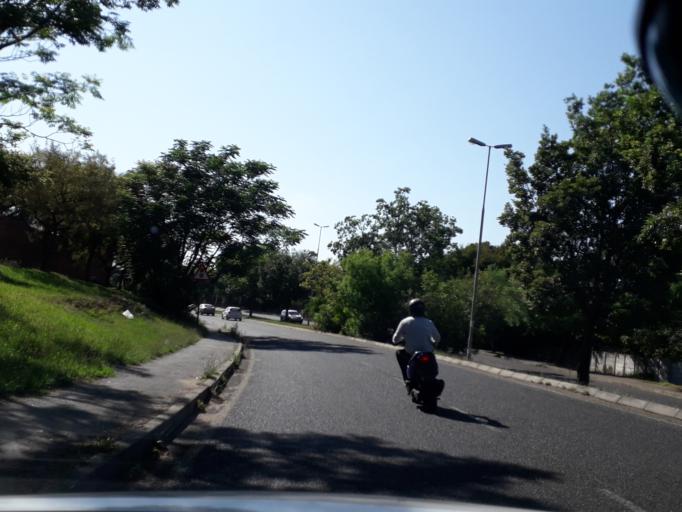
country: ZA
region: Gauteng
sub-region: City of Johannesburg Metropolitan Municipality
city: Roodepoort
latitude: -26.0976
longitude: 27.9502
